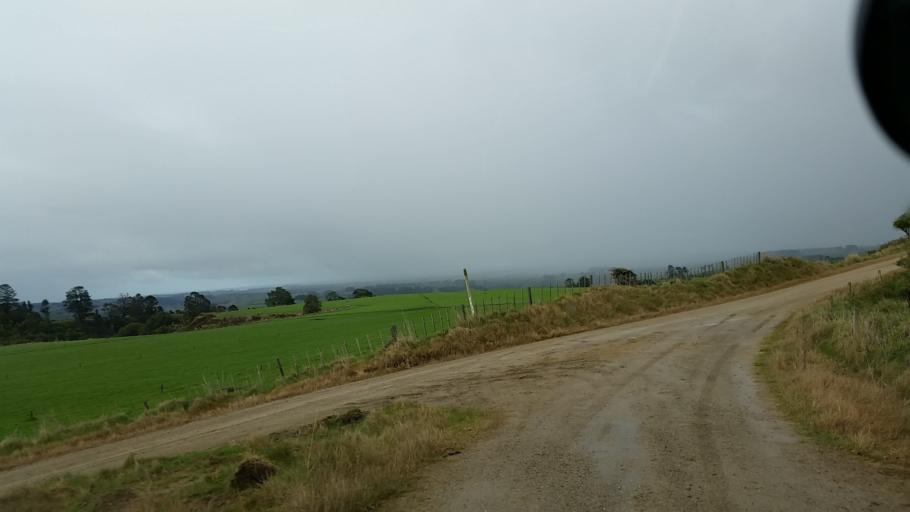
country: NZ
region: Taranaki
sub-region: South Taranaki District
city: Patea
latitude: -39.7240
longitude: 174.7159
